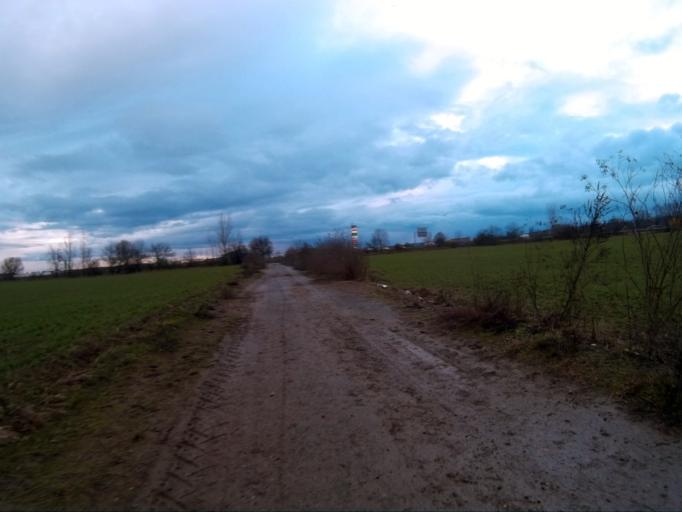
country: CZ
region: South Moravian
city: Modrice
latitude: 49.1450
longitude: 16.6354
